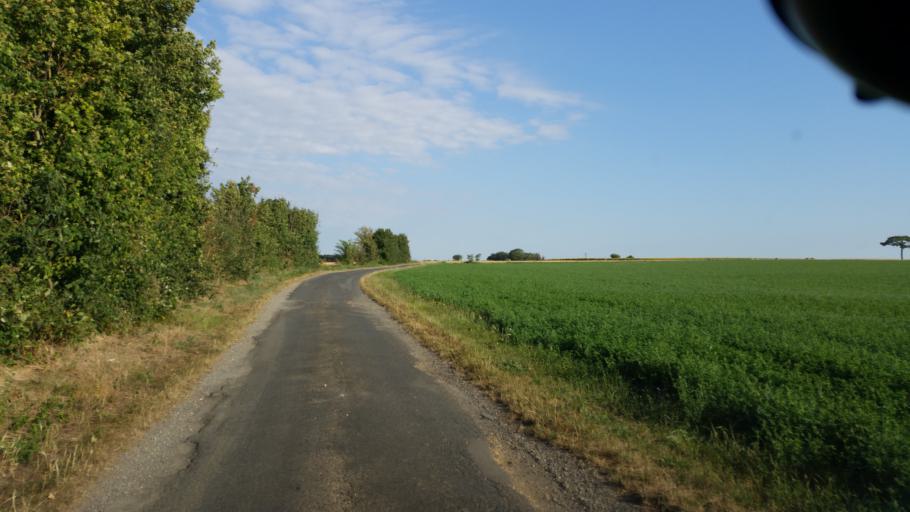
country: FR
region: Poitou-Charentes
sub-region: Departement de la Charente-Maritime
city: Saint-Jean-de-Liversay
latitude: 46.2314
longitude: -0.8891
